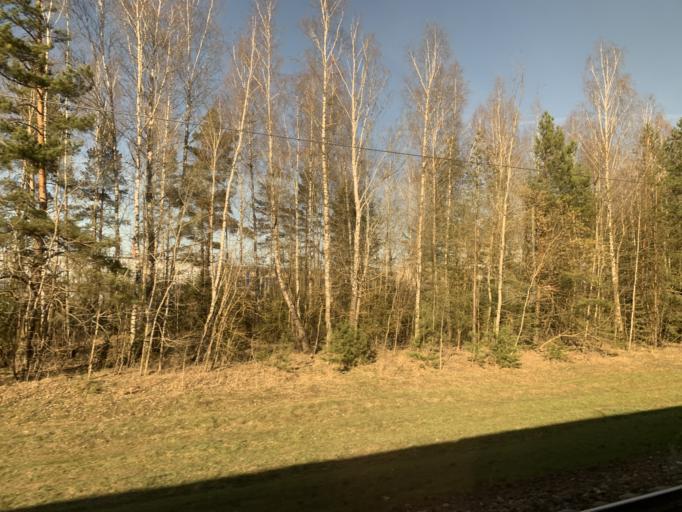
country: BY
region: Grodnenskaya
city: Smarhon'
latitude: 54.4384
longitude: 26.5091
